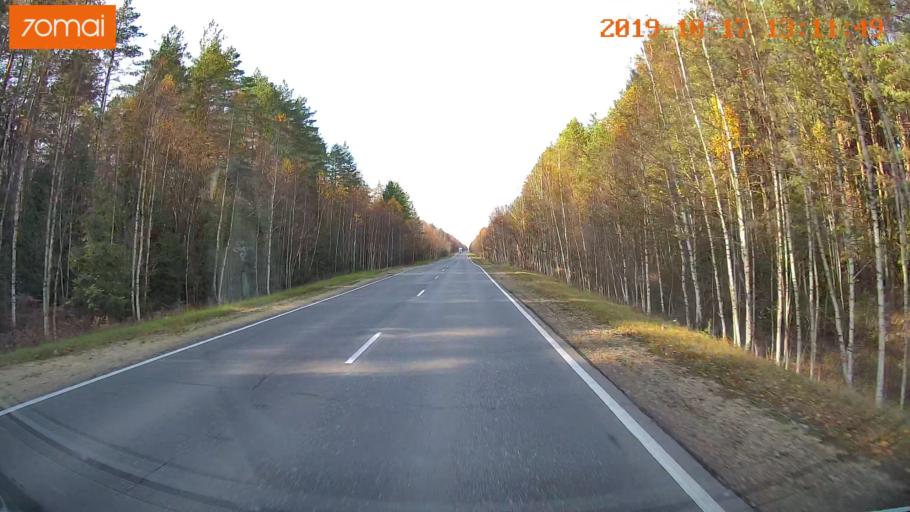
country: RU
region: Rjazan
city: Gus'-Zheleznyy
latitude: 55.0309
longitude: 41.2268
